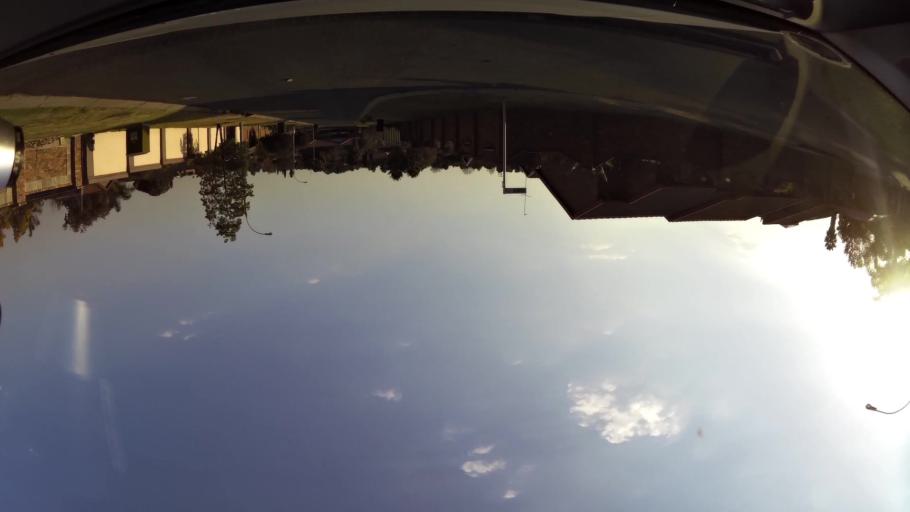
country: ZA
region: Gauteng
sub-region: City of Johannesburg Metropolitan Municipality
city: Modderfontein
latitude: -26.0748
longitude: 28.2236
